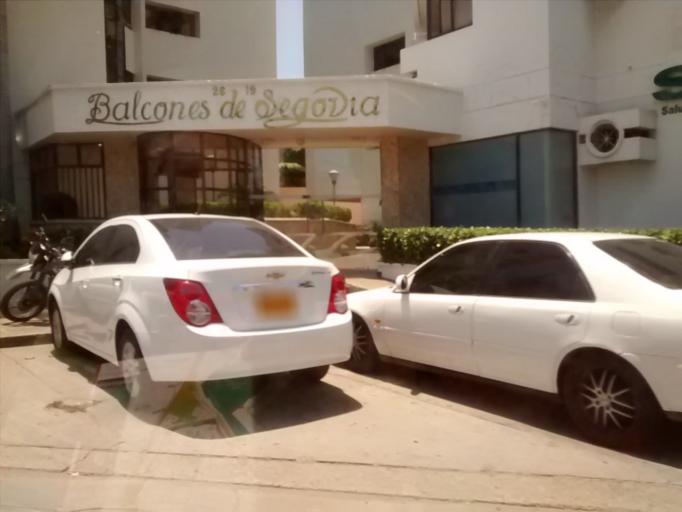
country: CO
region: Bolivar
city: Cartagena
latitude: 10.4168
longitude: -75.5421
